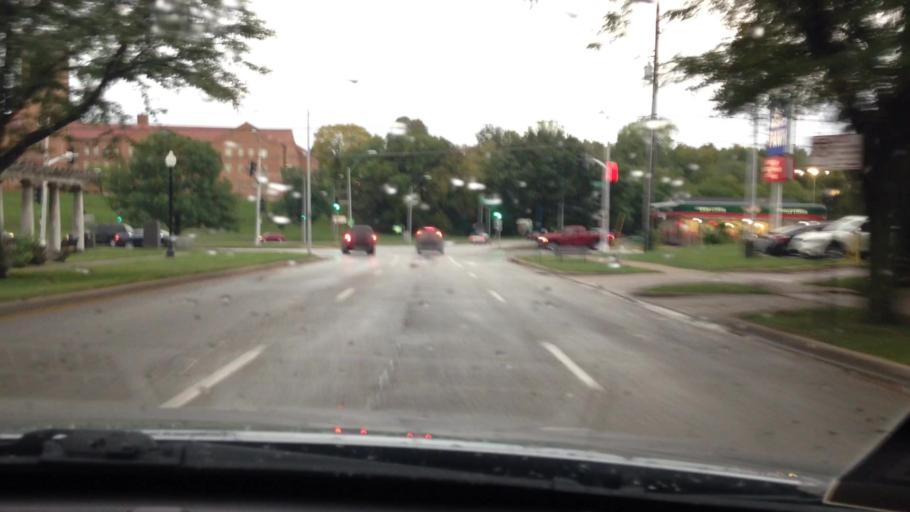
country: US
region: Kansas
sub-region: Johnson County
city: Mission Hills
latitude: 39.0138
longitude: -94.5704
